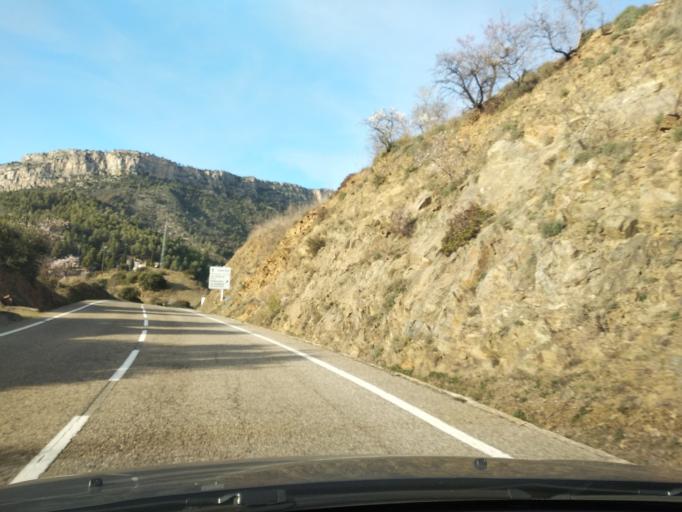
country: ES
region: Catalonia
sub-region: Provincia de Tarragona
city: Margalef
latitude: 41.2196
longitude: 0.7648
